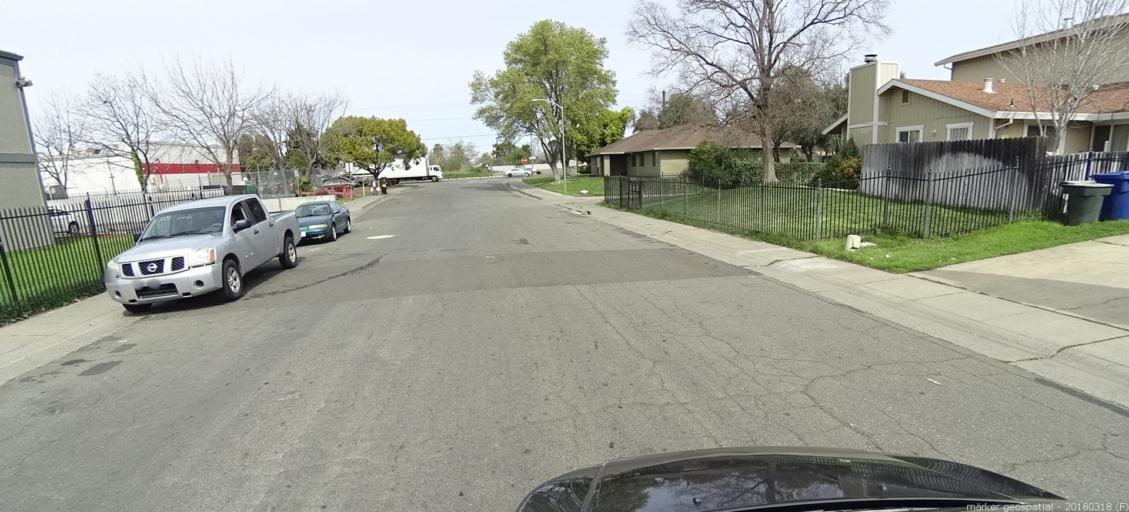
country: US
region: California
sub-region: Sacramento County
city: Parkway
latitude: 38.5241
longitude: -121.4572
